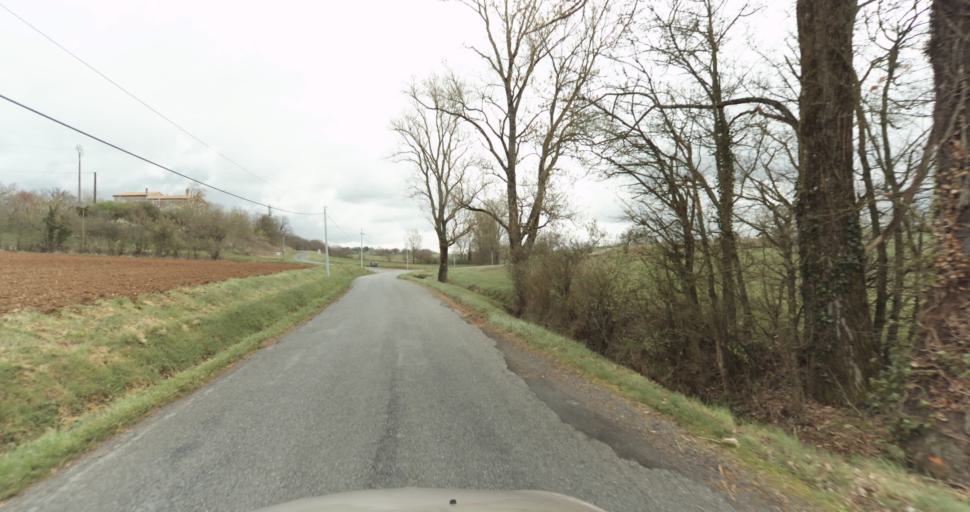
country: FR
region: Midi-Pyrenees
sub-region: Departement du Tarn
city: Frejairolles
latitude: 43.8561
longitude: 2.1932
